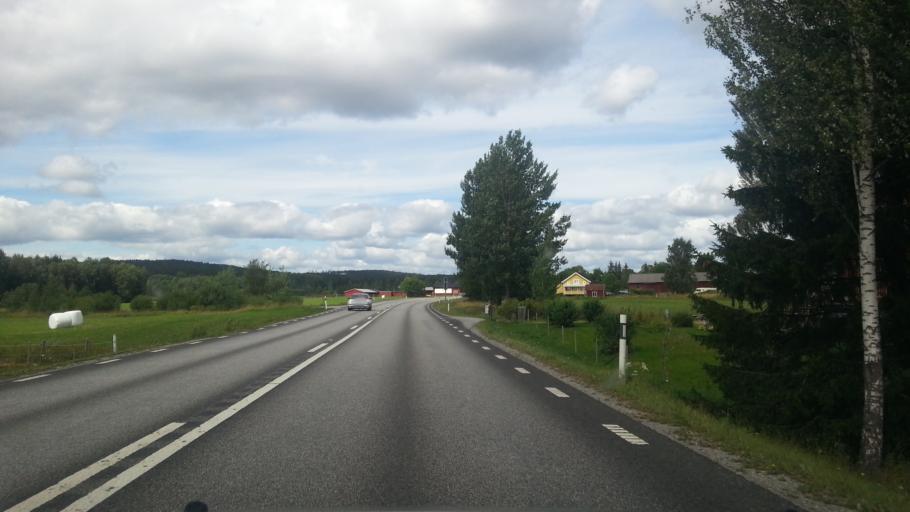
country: SE
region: OErebro
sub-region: Lindesbergs Kommun
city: Lindesberg
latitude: 59.6256
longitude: 15.1797
